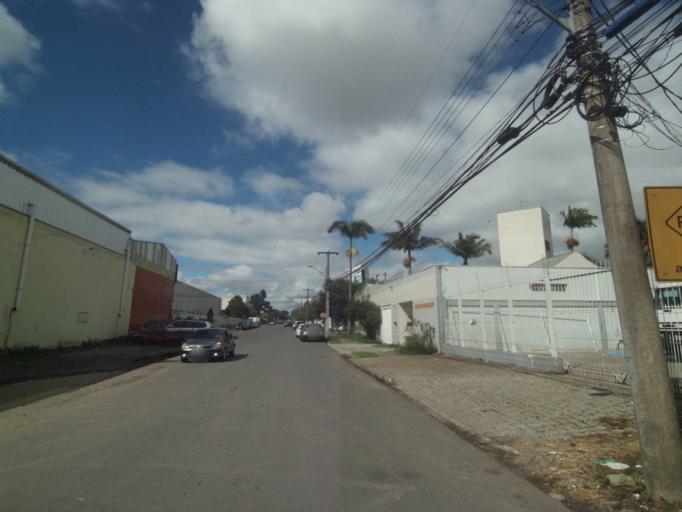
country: BR
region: Parana
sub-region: Curitiba
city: Curitiba
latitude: -25.4721
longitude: -49.2584
